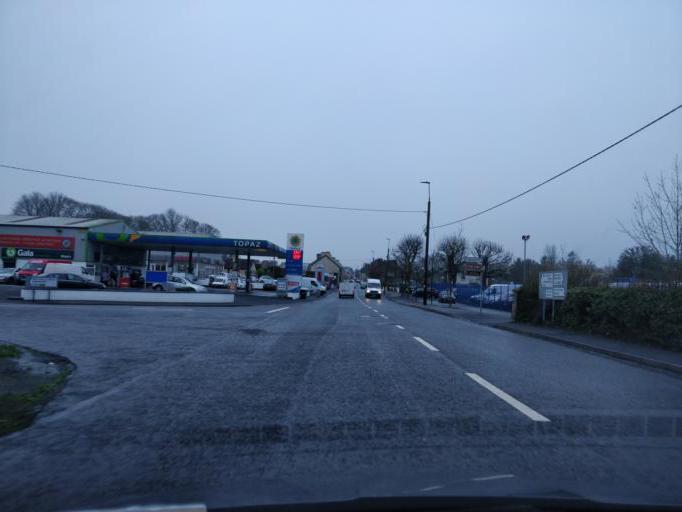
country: IE
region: Connaught
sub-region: Maigh Eo
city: Kiltamagh
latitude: 53.8544
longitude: -8.9950
